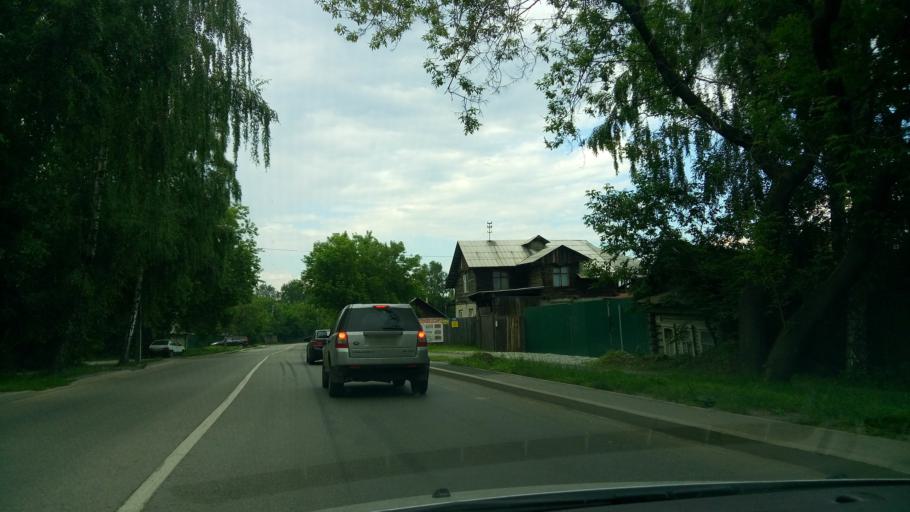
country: RU
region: Sverdlovsk
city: Yekaterinburg
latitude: 56.8799
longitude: 60.6928
